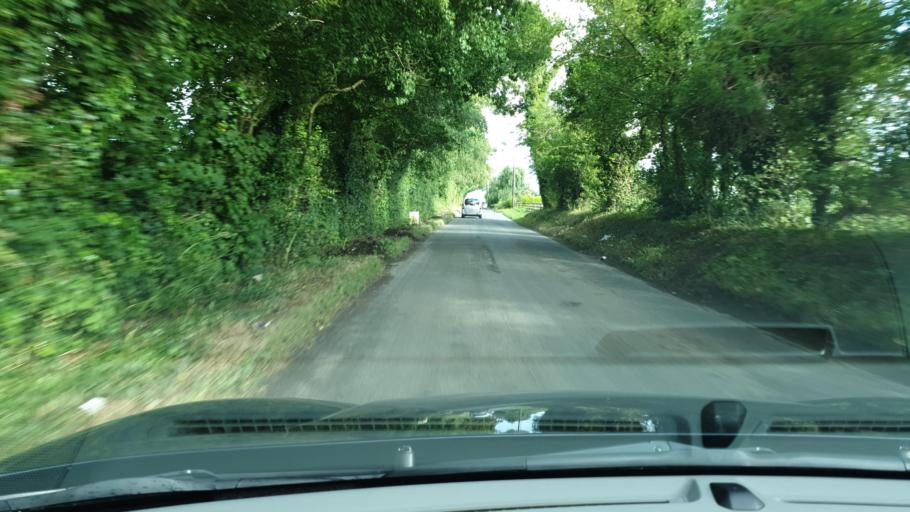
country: IE
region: Leinster
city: Balrothery
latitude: 53.5680
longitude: -6.1512
